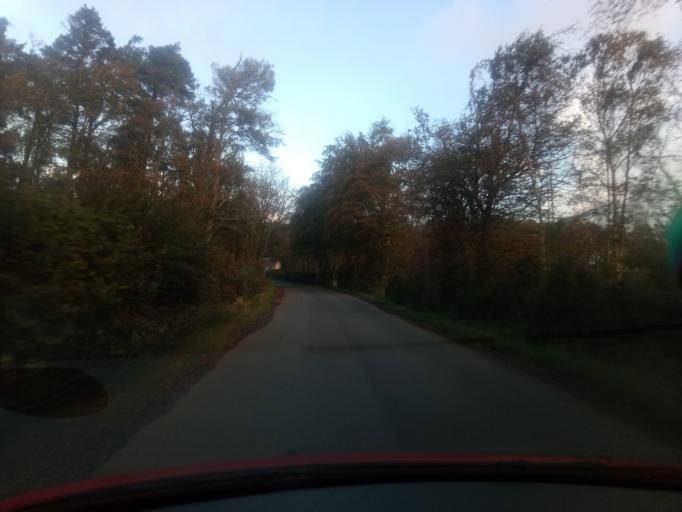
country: GB
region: Scotland
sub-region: The Scottish Borders
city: Jedburgh
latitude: 55.3872
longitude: -2.6432
